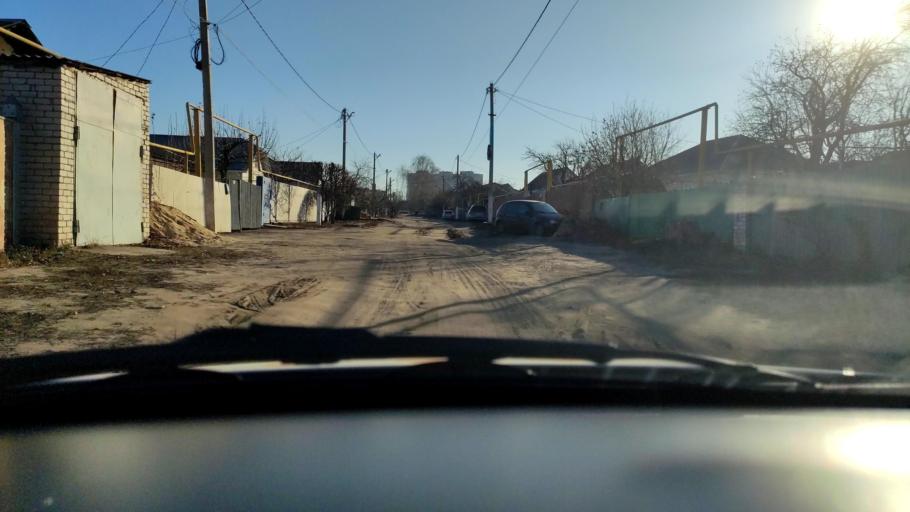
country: RU
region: Voronezj
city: Podgornoye
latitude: 51.7304
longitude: 39.1553
